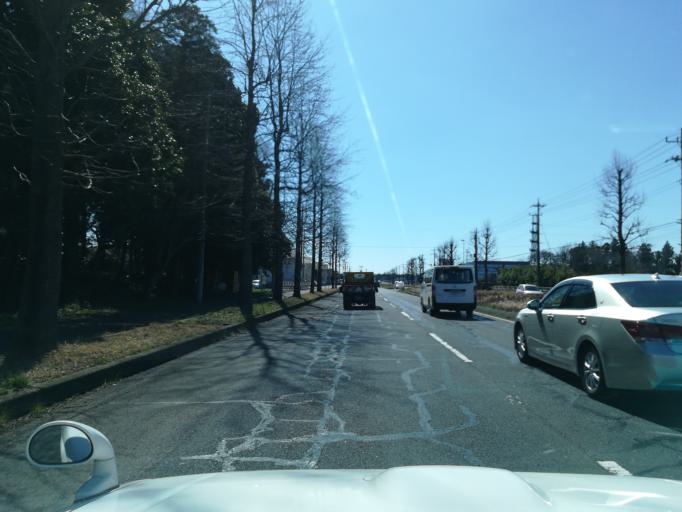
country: JP
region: Ibaraki
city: Naka
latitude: 36.0146
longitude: 140.1455
